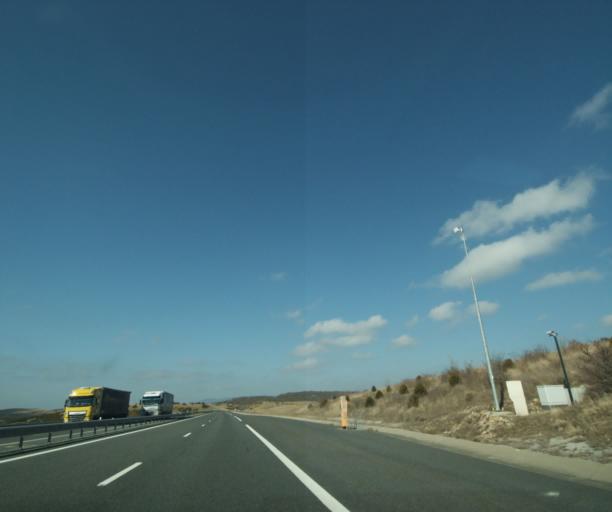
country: FR
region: Midi-Pyrenees
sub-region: Departement de l'Aveyron
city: Creissels
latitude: 44.0565
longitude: 3.0384
